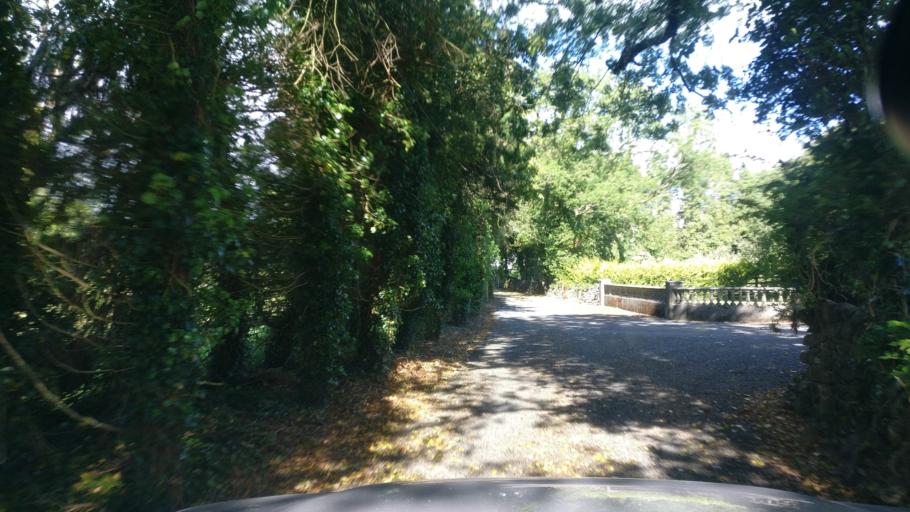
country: IE
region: Connaught
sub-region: County Galway
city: Loughrea
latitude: 53.2420
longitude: -8.6161
